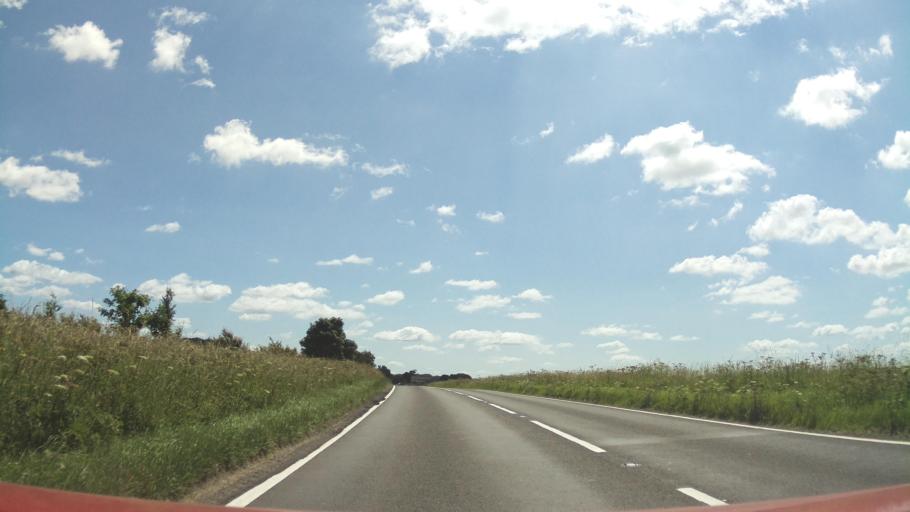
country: GB
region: England
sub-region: Derbyshire
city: Bakewell
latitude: 53.1541
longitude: -1.7701
